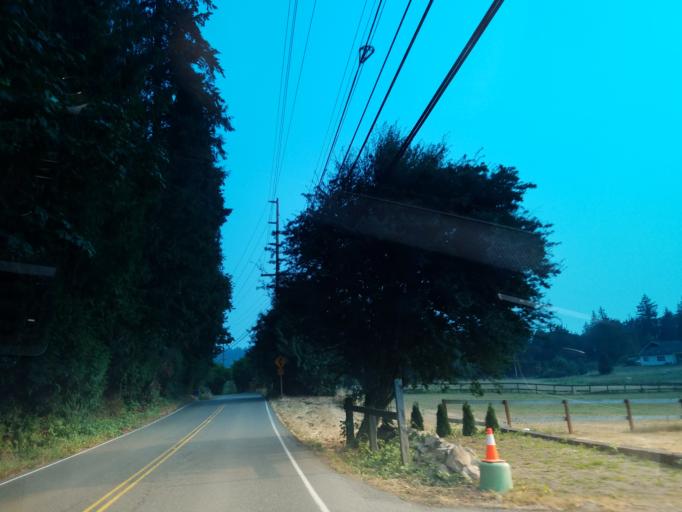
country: US
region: Washington
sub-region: King County
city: Sammamish
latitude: 47.6623
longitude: -122.0628
